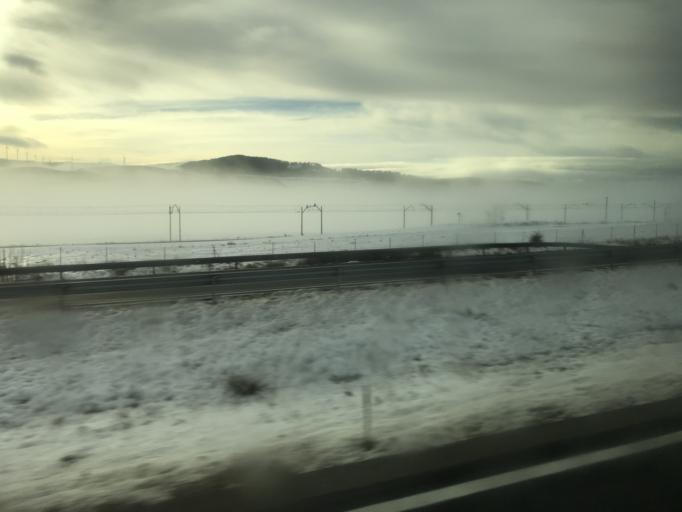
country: ES
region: Castille and Leon
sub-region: Provincia de Burgos
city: Santa Olalla de Bureba
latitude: 42.4711
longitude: -3.4450
